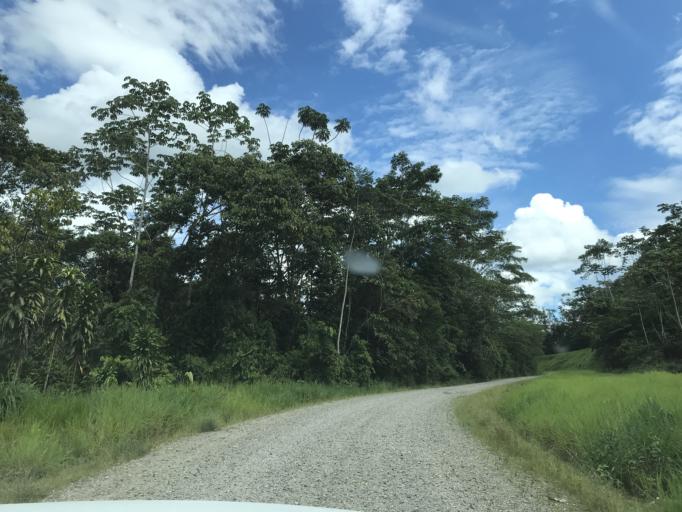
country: EC
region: Orellana
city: Puerto Francisco de Orellana
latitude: -0.6131
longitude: -76.4653
